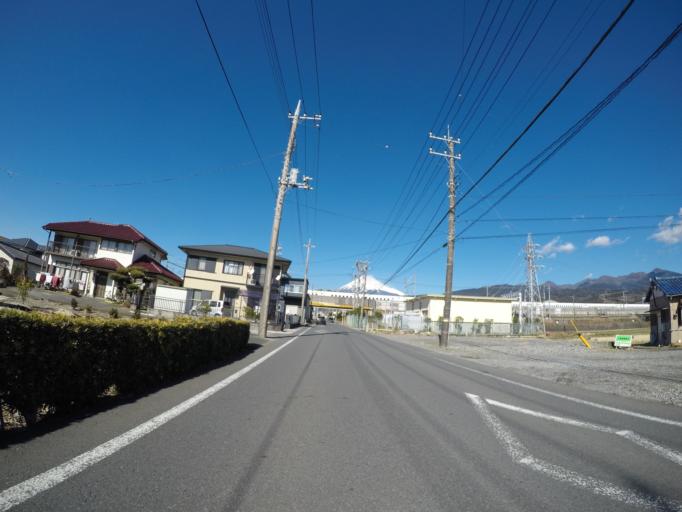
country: JP
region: Shizuoka
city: Fuji
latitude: 35.1540
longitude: 138.7416
